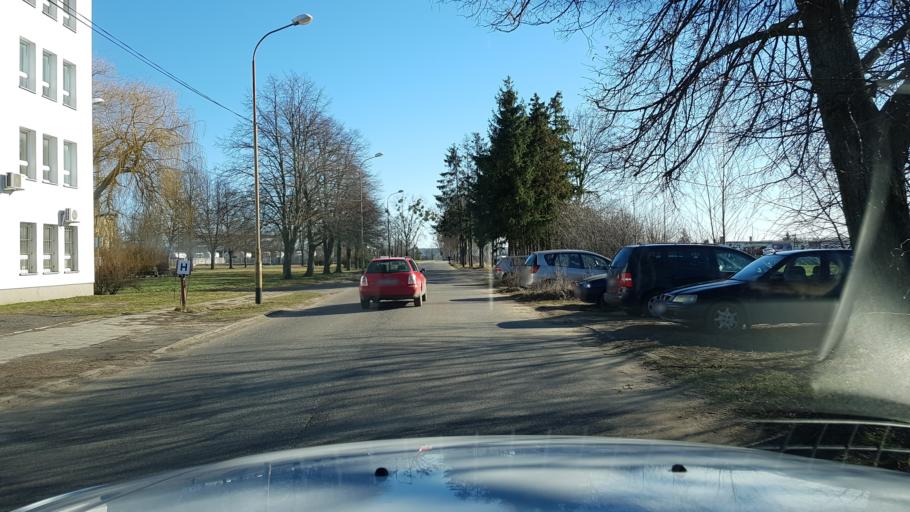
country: PL
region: West Pomeranian Voivodeship
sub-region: Powiat mysliborski
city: Barlinek
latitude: 52.9937
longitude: 15.1906
